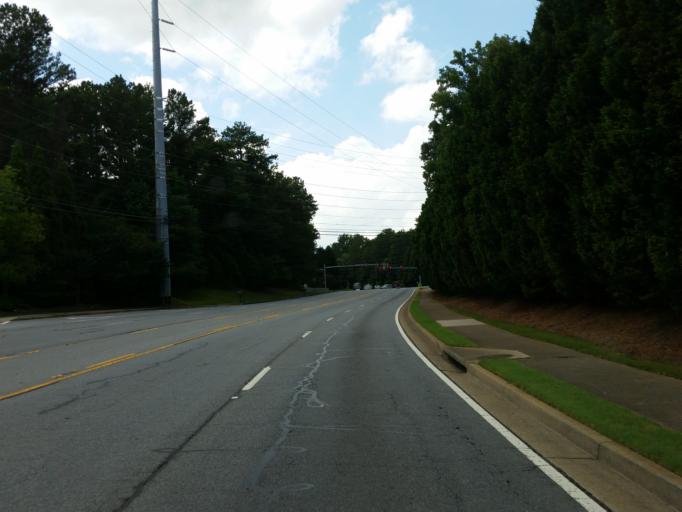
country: US
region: Georgia
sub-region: Fulton County
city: Roswell
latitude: 34.0284
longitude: -84.4310
